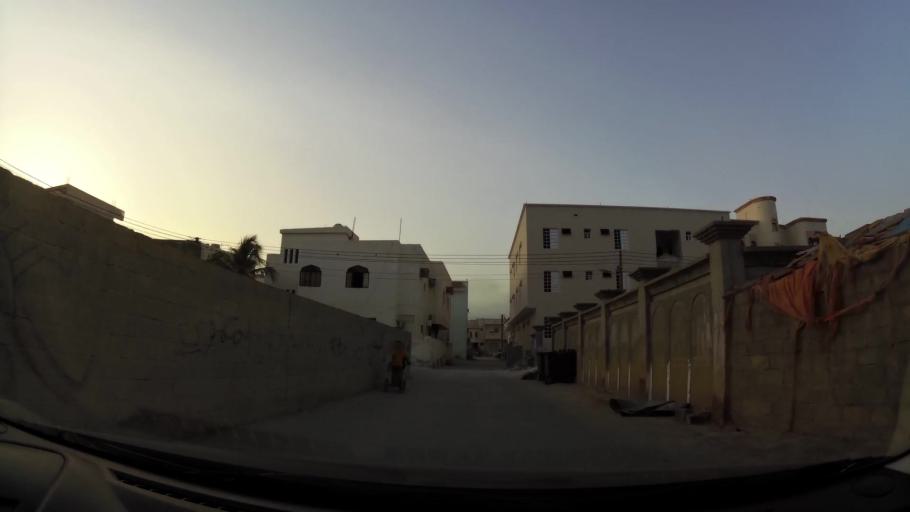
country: OM
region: Zufar
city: Salalah
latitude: 17.0199
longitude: 54.1256
